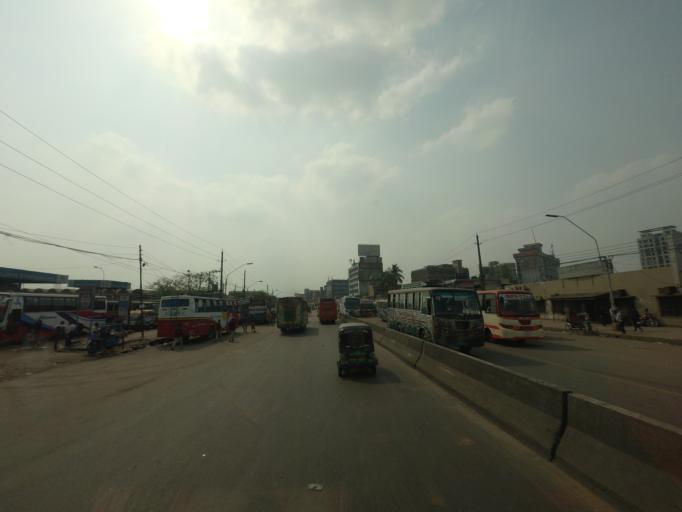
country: BD
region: Dhaka
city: Azimpur
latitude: 23.7832
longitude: 90.3447
